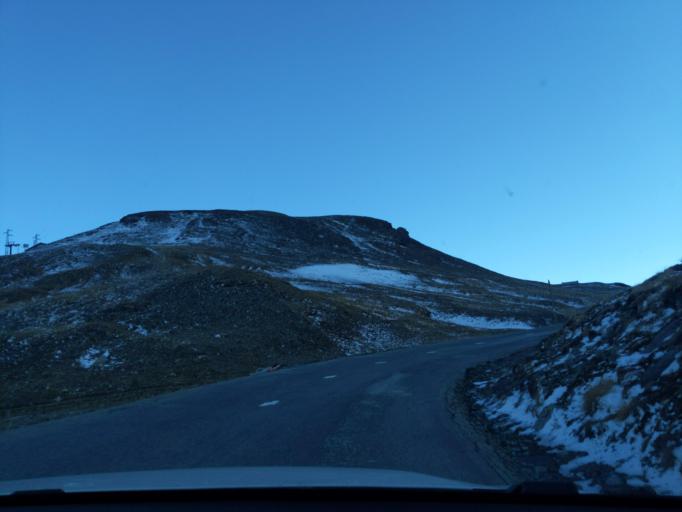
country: FR
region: Rhone-Alpes
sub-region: Departement de la Savoie
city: Val-d'Isere
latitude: 45.4231
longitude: 7.0285
